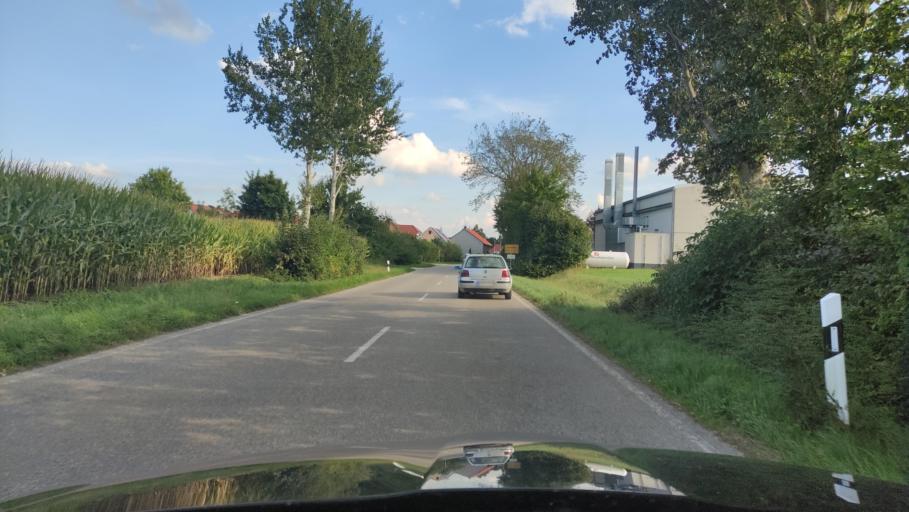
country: DE
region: Bavaria
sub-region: Swabia
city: Breitenthal
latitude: 48.2392
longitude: 10.2909
